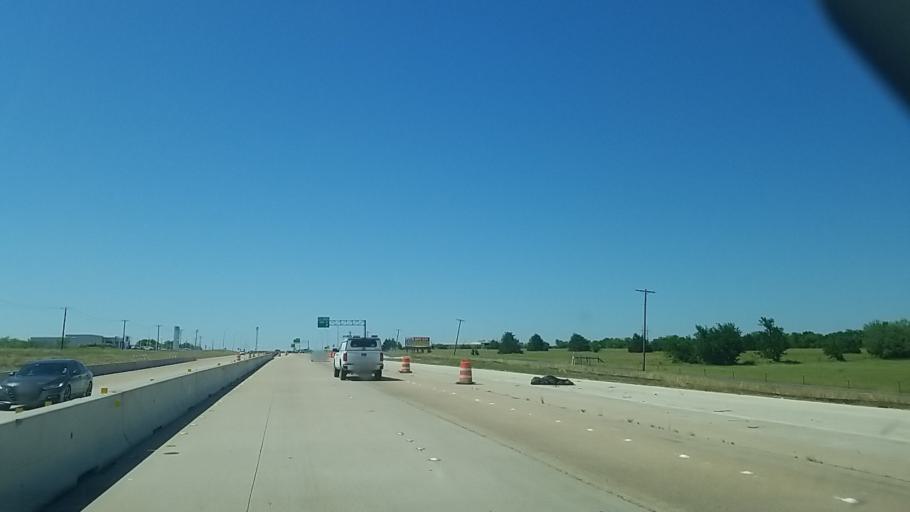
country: US
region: Texas
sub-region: Navarro County
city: Corsicana
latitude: 32.0532
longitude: -96.4501
